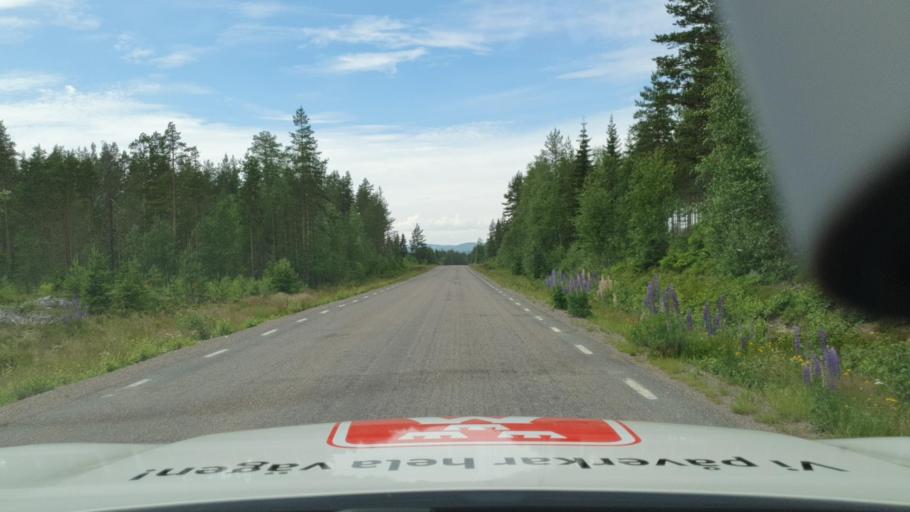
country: NO
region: Hedmark
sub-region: Grue
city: Kirkenaer
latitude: 60.6825
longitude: 12.6519
